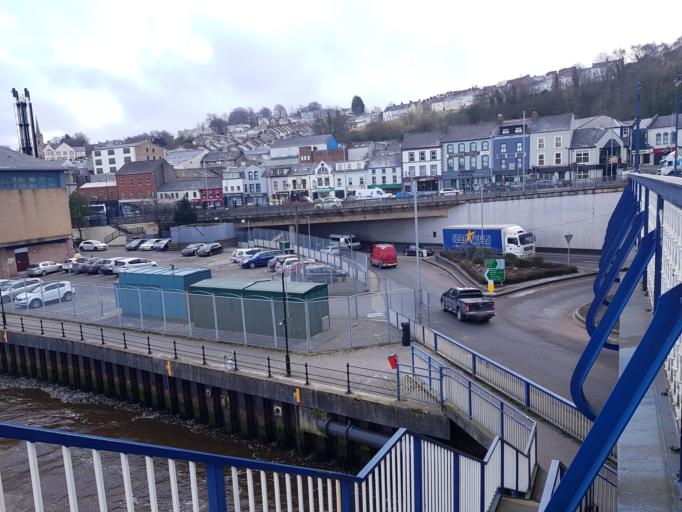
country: GB
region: Northern Ireland
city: Londonderry County Borough
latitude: 54.9900
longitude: -7.3166
